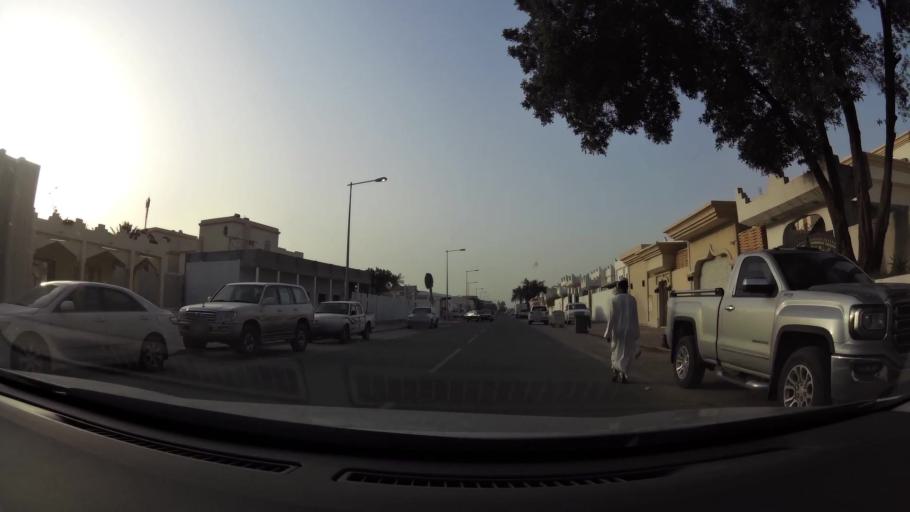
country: QA
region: Baladiyat ar Rayyan
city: Ar Rayyan
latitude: 25.2362
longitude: 51.4474
